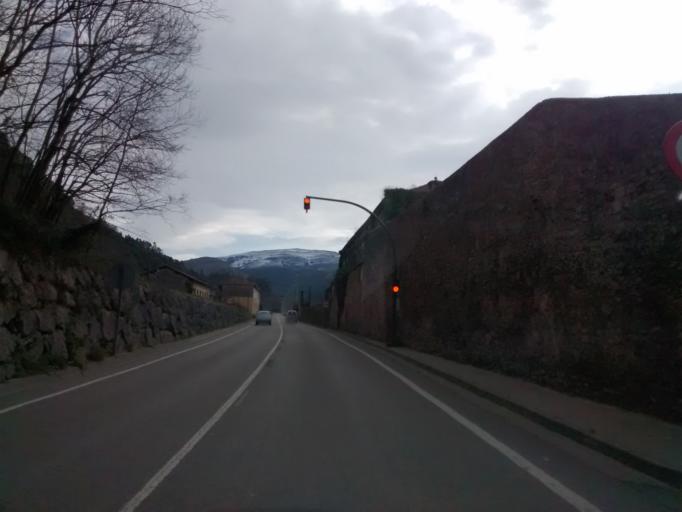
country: ES
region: Cantabria
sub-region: Provincia de Cantabria
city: Entrambasaguas
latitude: 43.3619
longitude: -3.7127
